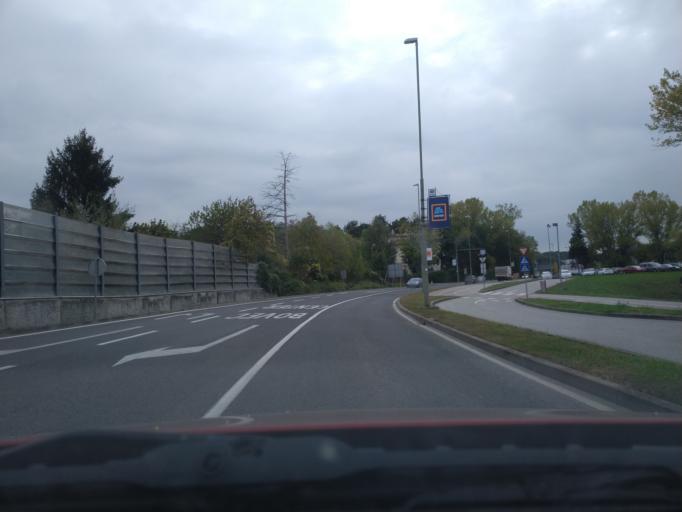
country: SI
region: Nova Gorica
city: Nova Gorica
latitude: 45.9579
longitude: 13.6528
